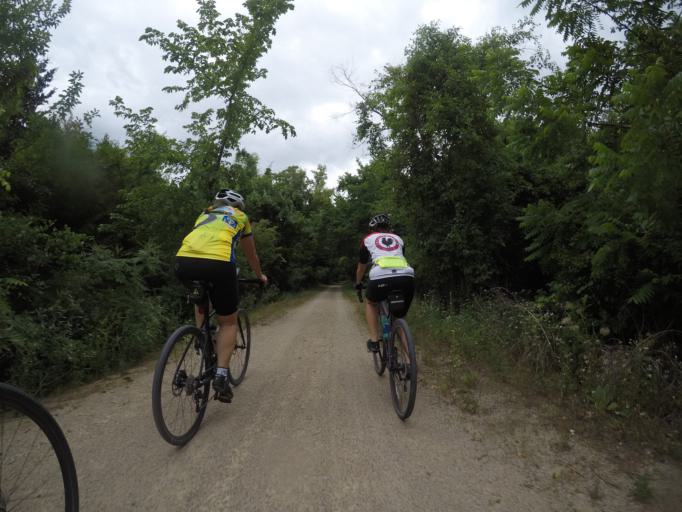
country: US
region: Kansas
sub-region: Anderson County
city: Garnett
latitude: 38.2404
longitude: -95.2588
